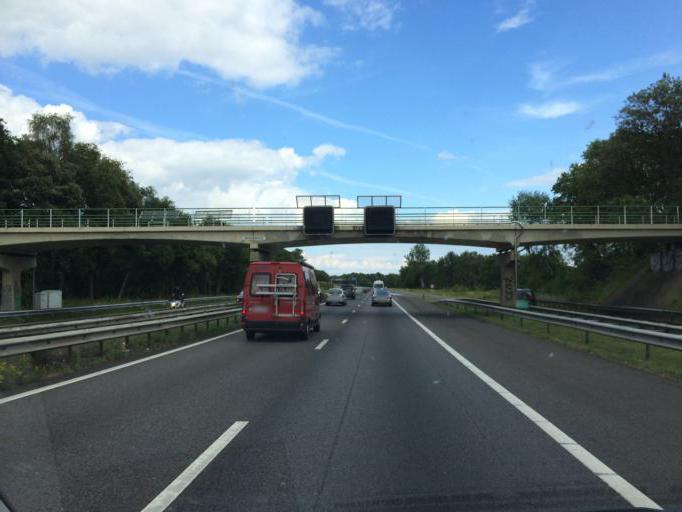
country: NL
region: North Brabant
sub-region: Gemeente Geldrop-Mierlo
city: Geldrop
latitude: 51.4048
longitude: 5.5423
